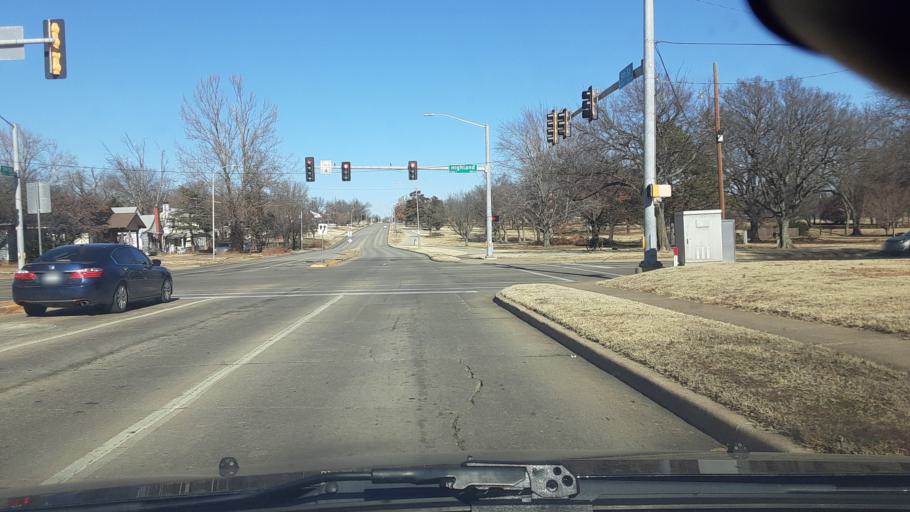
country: US
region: Oklahoma
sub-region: Kay County
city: Ponca City
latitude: 36.7094
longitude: -97.0783
